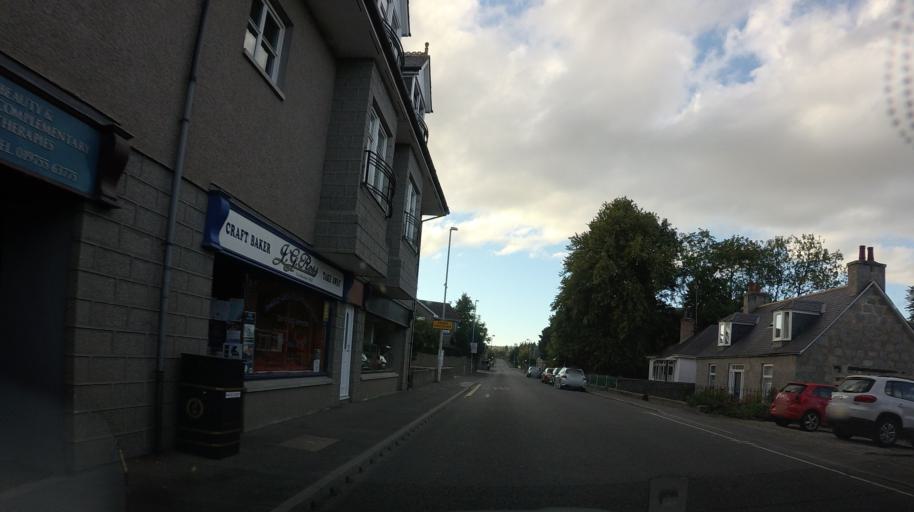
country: GB
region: Scotland
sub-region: Aberdeenshire
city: Alford
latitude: 57.2325
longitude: -2.7030
